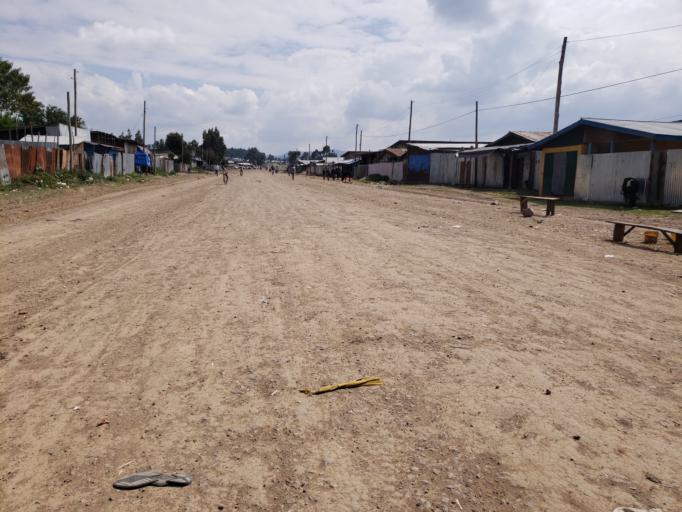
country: ET
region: Oromiya
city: Dodola
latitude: 7.0040
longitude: 39.3917
